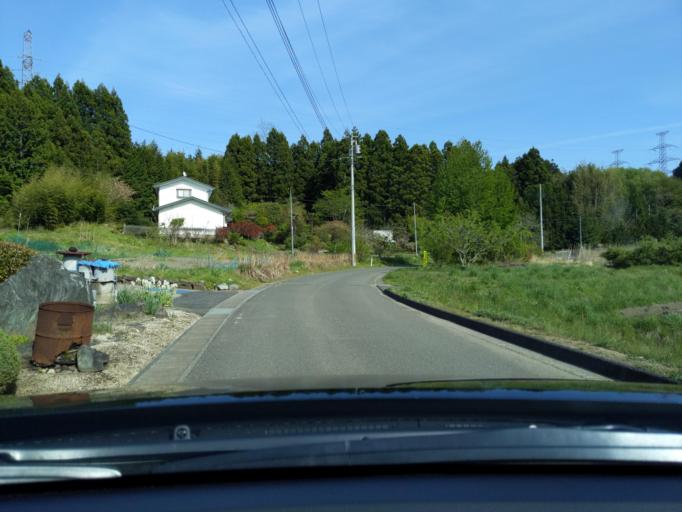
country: JP
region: Fukushima
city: Sukagawa
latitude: 37.3119
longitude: 140.4252
